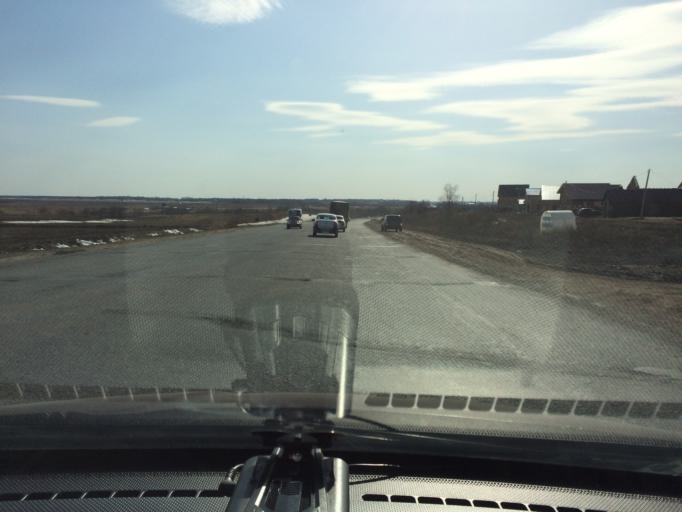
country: RU
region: Mariy-El
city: Yoshkar-Ola
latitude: 56.6925
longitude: 48.0537
